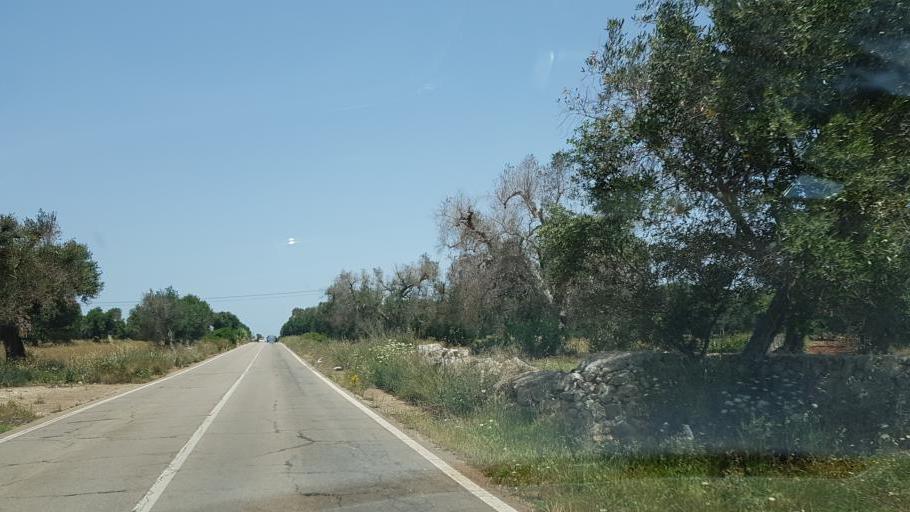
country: IT
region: Apulia
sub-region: Provincia di Lecce
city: Porto Cesareo
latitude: 40.2898
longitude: 17.9129
